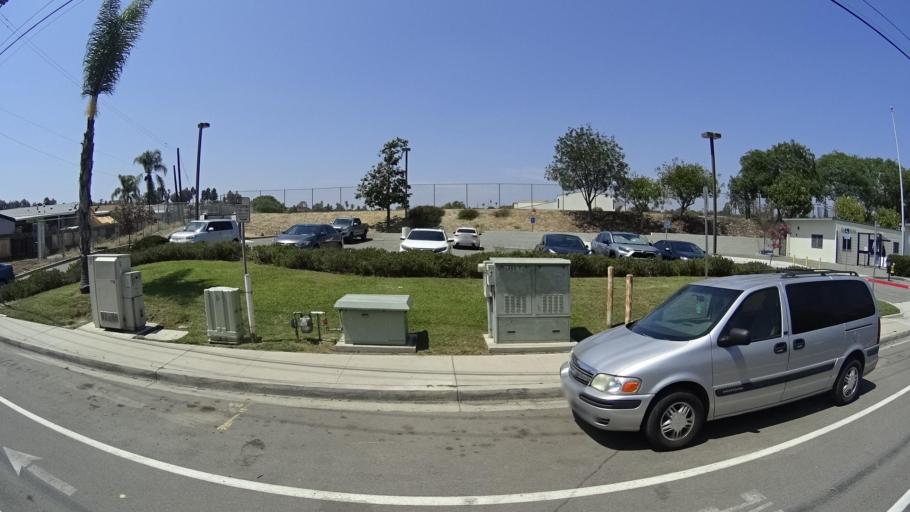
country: US
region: California
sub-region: San Diego County
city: Vista
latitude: 33.2030
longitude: -117.2552
